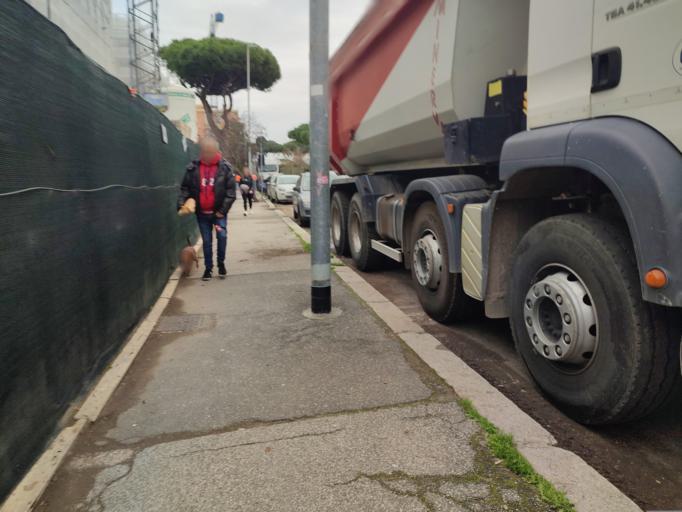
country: IT
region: Latium
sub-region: Citta metropolitana di Roma Capitale
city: Lido di Ostia
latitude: 41.7357
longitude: 12.2882
